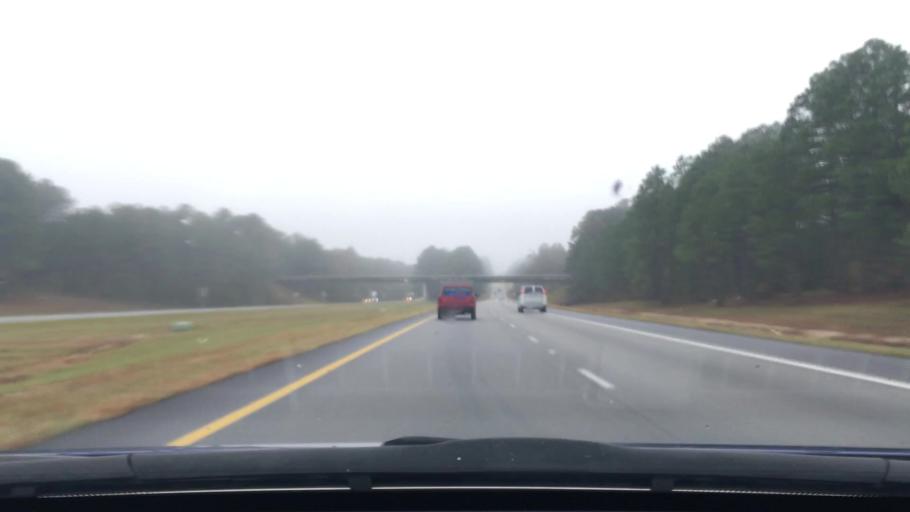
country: US
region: South Carolina
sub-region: Kershaw County
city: Camden
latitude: 34.2082
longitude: -80.4515
